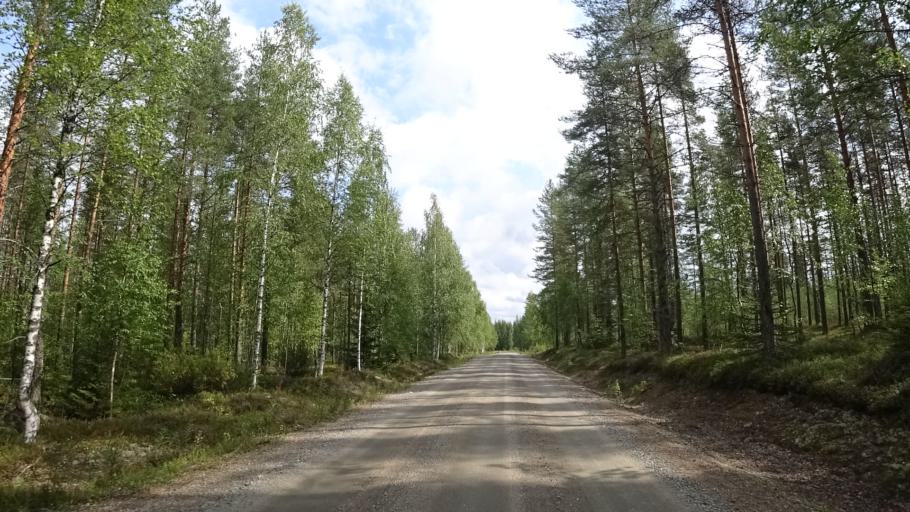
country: FI
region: North Karelia
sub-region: Joensuu
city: Ilomantsi
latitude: 62.9266
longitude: 31.3850
